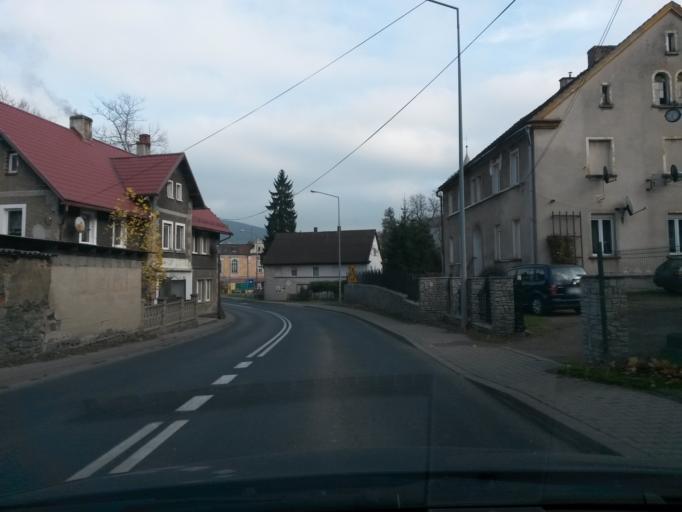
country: PL
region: Lower Silesian Voivodeship
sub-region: Powiat jeleniogorski
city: Janowice Wielkie
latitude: 50.9084
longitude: 15.9562
